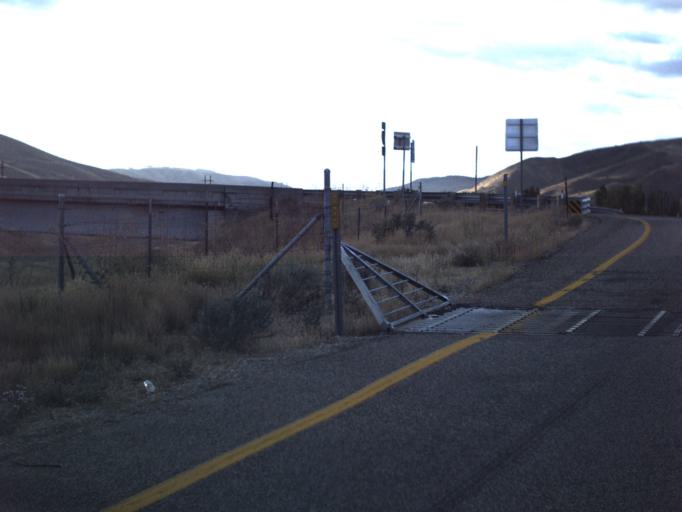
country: US
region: Utah
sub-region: Summit County
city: Coalville
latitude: 41.0162
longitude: -111.4909
